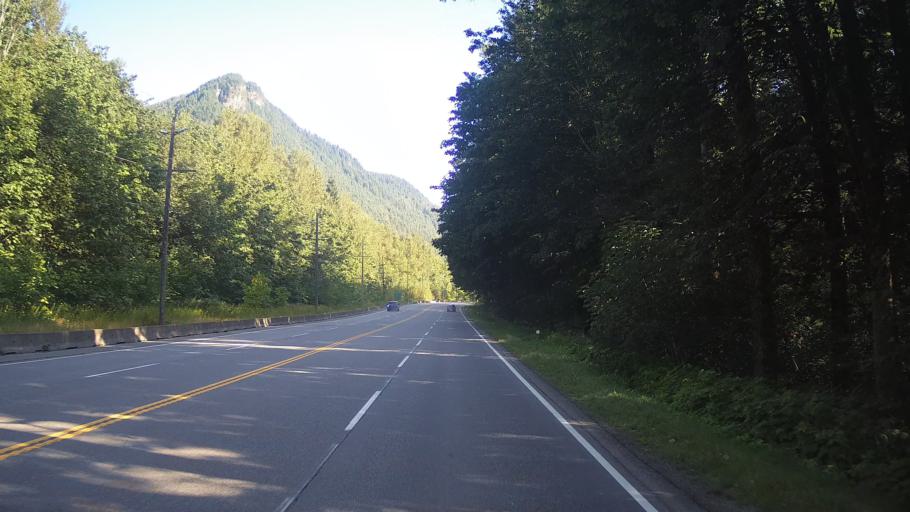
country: CA
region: British Columbia
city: Hope
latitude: 49.4454
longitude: -121.4369
